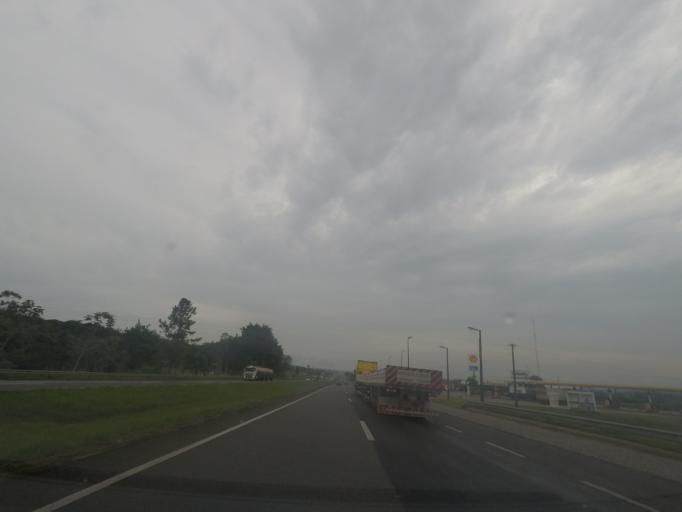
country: BR
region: Sao Paulo
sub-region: Pariquera-Acu
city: Pariquera Acu
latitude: -24.6255
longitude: -47.8988
